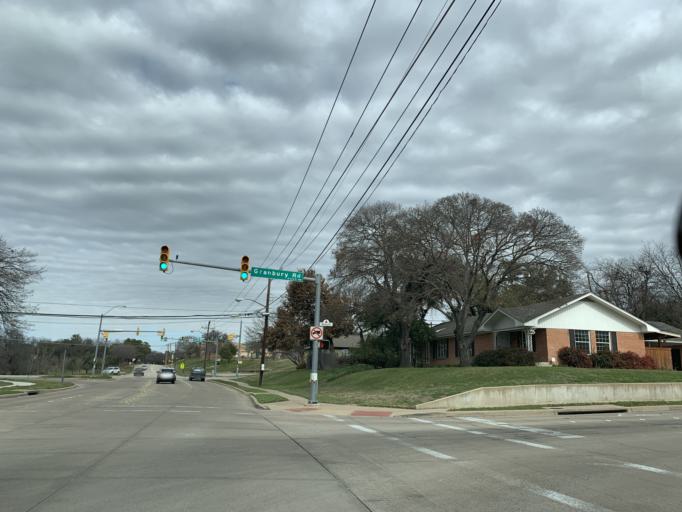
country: US
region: Texas
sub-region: Tarrant County
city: Edgecliff Village
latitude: 32.6837
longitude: -97.3734
